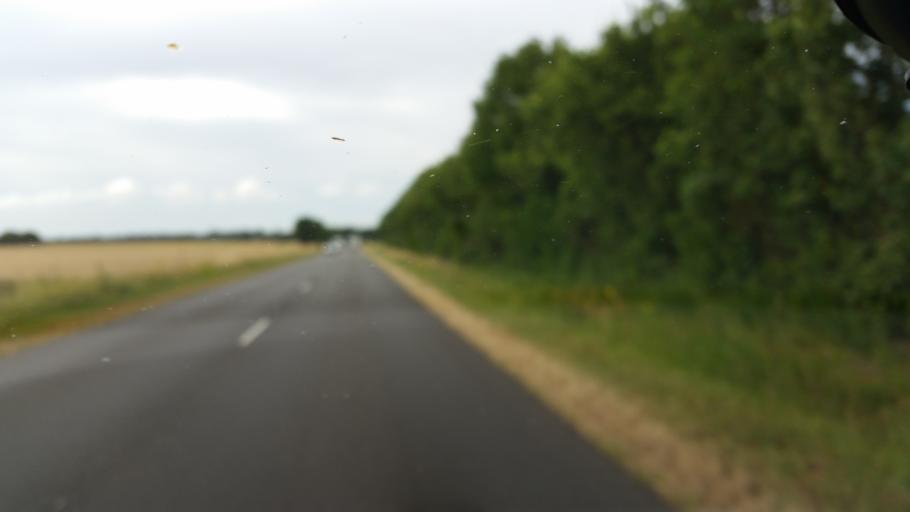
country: FR
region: Poitou-Charentes
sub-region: Departement de la Charente-Maritime
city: Surgeres
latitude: 46.1474
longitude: -0.8073
